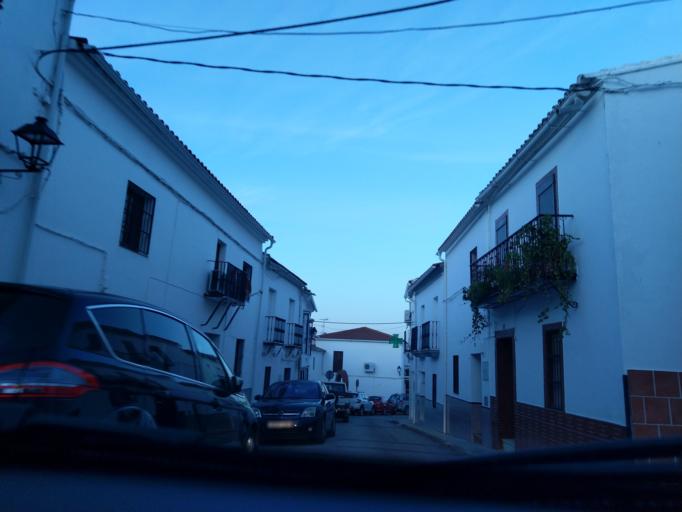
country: ES
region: Extremadura
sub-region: Provincia de Badajoz
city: Reina
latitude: 38.1519
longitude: -5.8978
